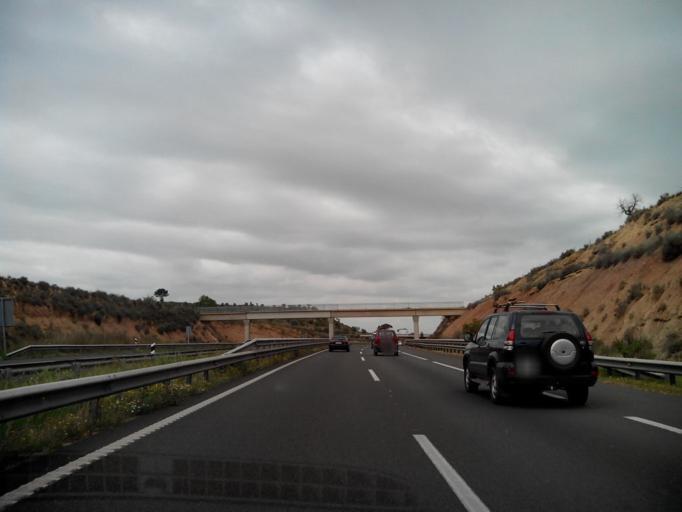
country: ES
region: Catalonia
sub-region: Provincia de Lleida
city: Tarrega
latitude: 41.6584
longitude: 1.1286
